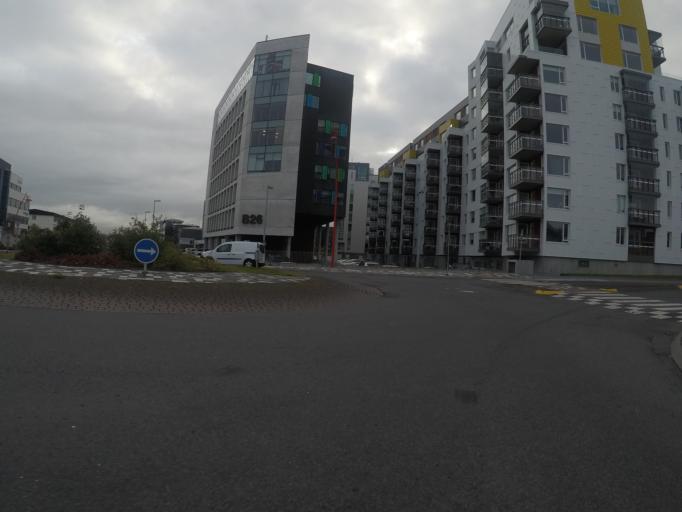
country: IS
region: Capital Region
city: Reykjavik
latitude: 64.1457
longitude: -21.9010
